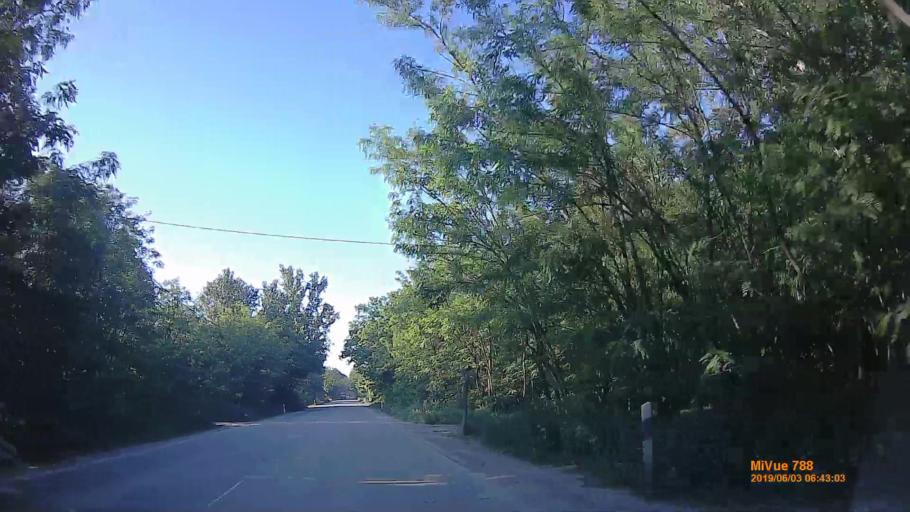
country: HU
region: Pest
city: Delegyhaza
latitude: 47.2597
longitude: 19.1212
